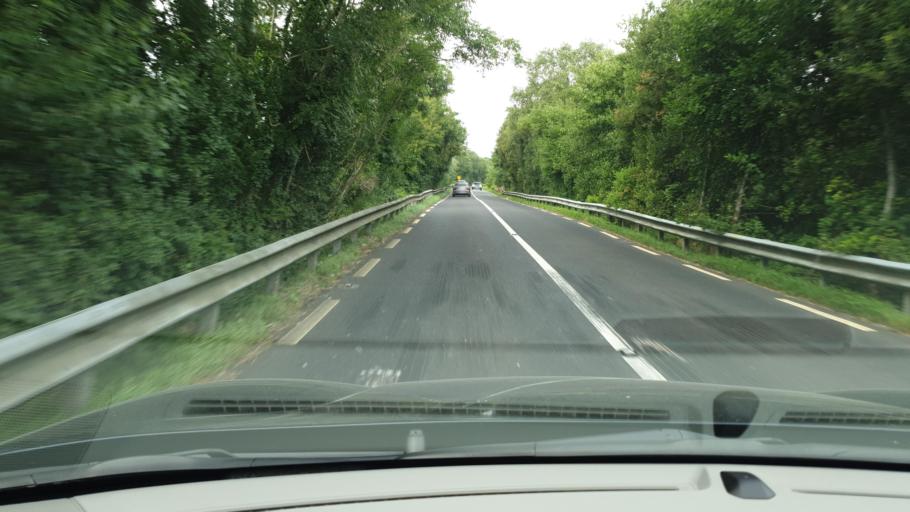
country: IE
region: Leinster
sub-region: An Mhi
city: Trim
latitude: 53.6347
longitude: -6.8177
